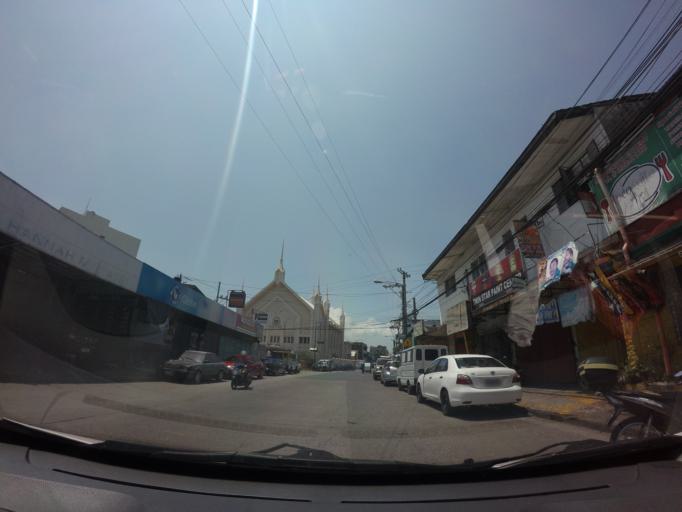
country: PH
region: Metro Manila
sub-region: Makati City
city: Makati City
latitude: 14.5613
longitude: 121.0007
